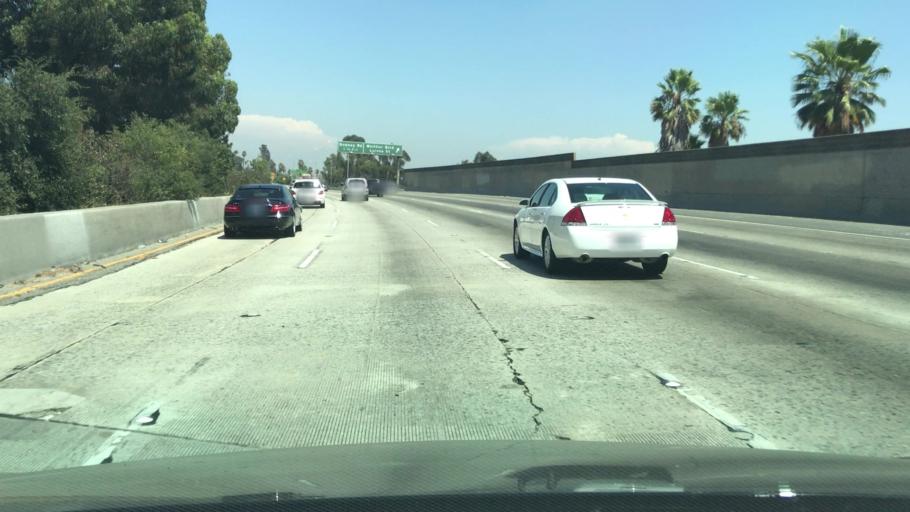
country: US
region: California
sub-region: Los Angeles County
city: Boyle Heights
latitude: 34.0281
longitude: -118.2088
